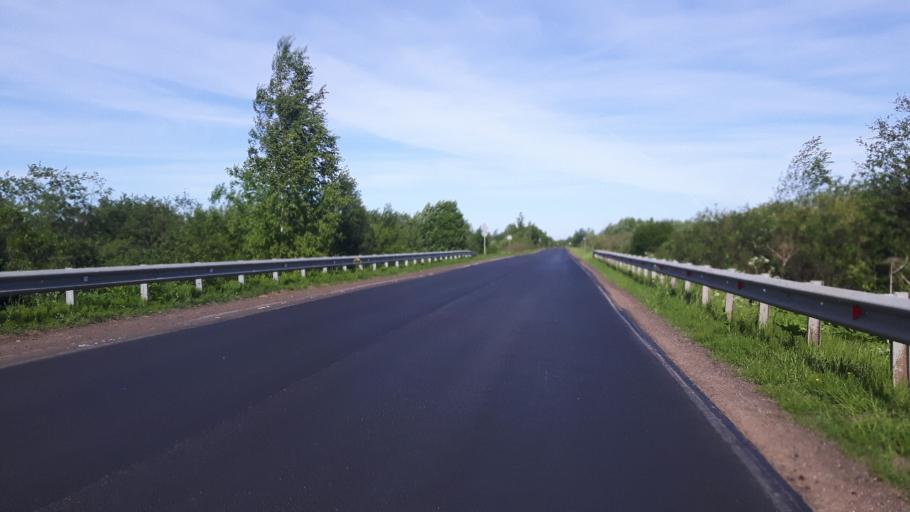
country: RU
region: Leningrad
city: Ivangorod
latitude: 59.4155
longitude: 28.3309
